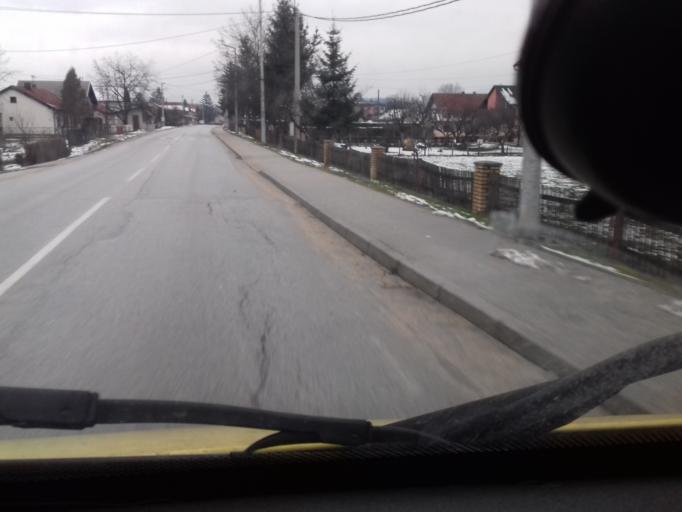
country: BA
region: Federation of Bosnia and Herzegovina
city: Vitez
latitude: 44.1626
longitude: 17.7790
